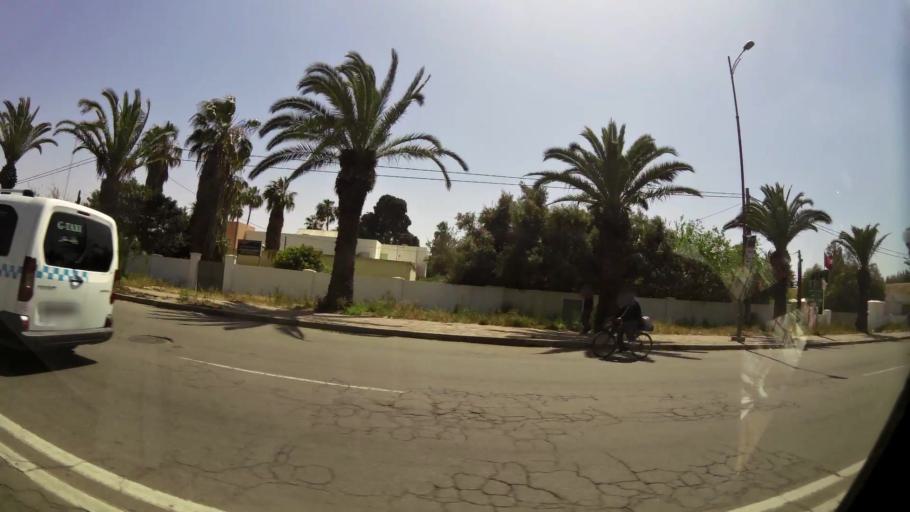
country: MA
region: Souss-Massa-Draa
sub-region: Inezgane-Ait Mellou
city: Inezgane
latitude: 30.3534
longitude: -9.5084
